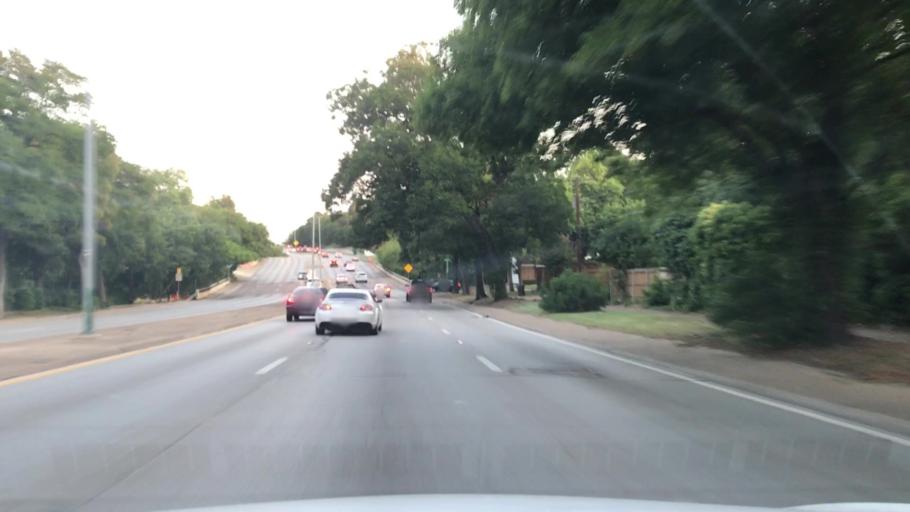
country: US
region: Texas
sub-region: Dallas County
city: Highland Park
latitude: 32.8194
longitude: -96.6910
